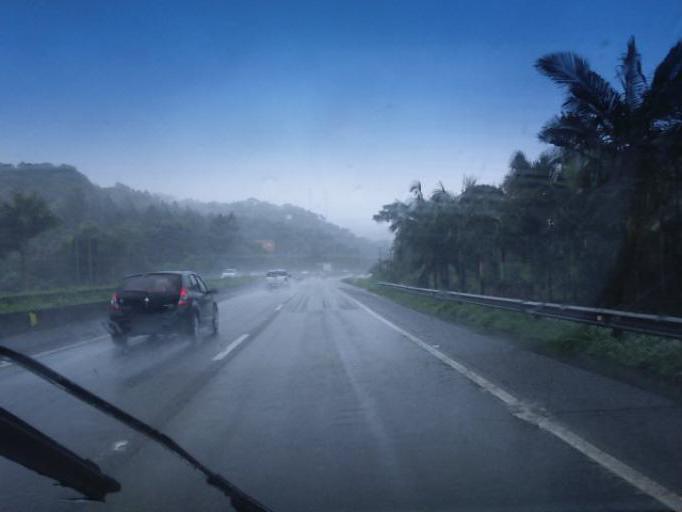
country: BR
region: Parana
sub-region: Guaratuba
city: Guaratuba
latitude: -25.9665
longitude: -48.8960
